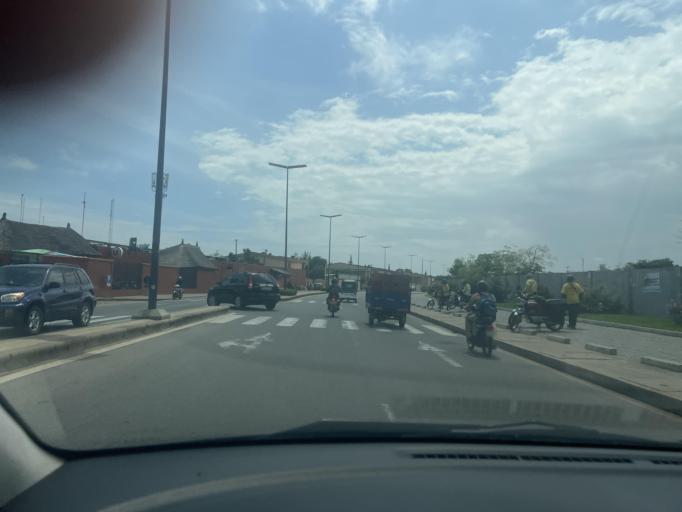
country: BJ
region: Littoral
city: Cotonou
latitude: 6.3500
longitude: 2.3868
